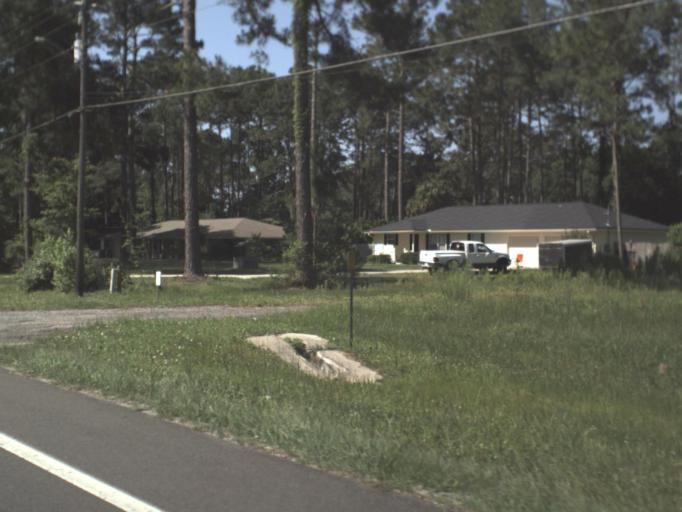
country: US
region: Florida
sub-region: Nassau County
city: Nassau Village-Ratliff
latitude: 30.5361
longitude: -81.7747
